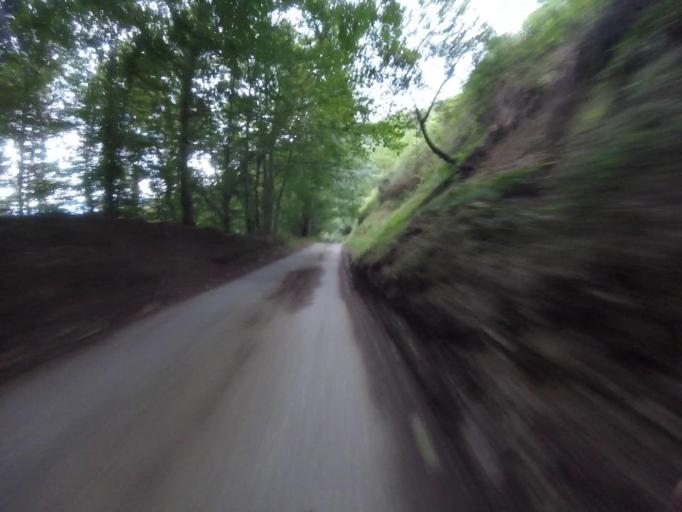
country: ES
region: Basque Country
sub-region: Provincia de Guipuzcoa
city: Errenteria
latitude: 43.2704
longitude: -1.8334
